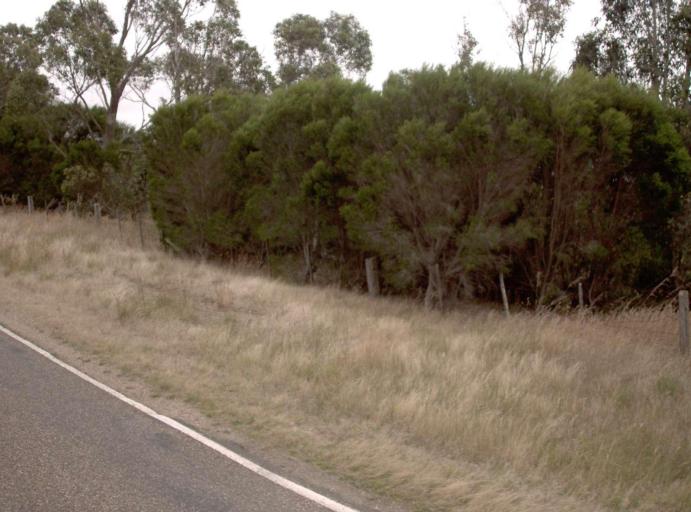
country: AU
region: Victoria
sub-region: Wellington
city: Heyfield
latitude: -38.1119
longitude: 146.7723
